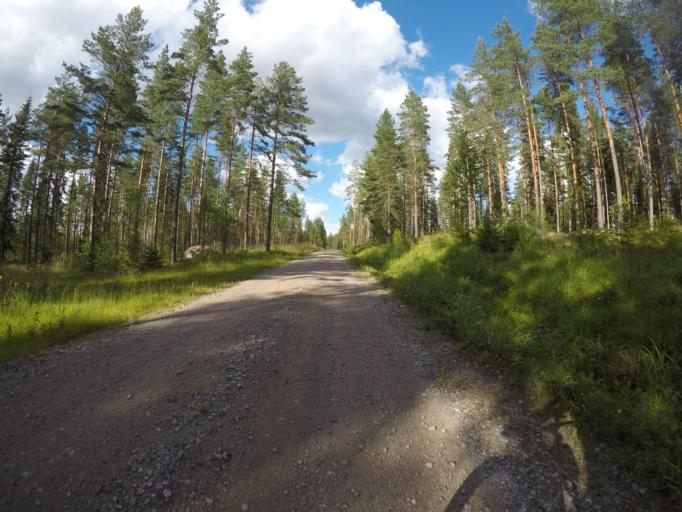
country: SE
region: OErebro
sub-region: Hallefors Kommun
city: Haellefors
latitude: 59.9233
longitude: 14.5642
